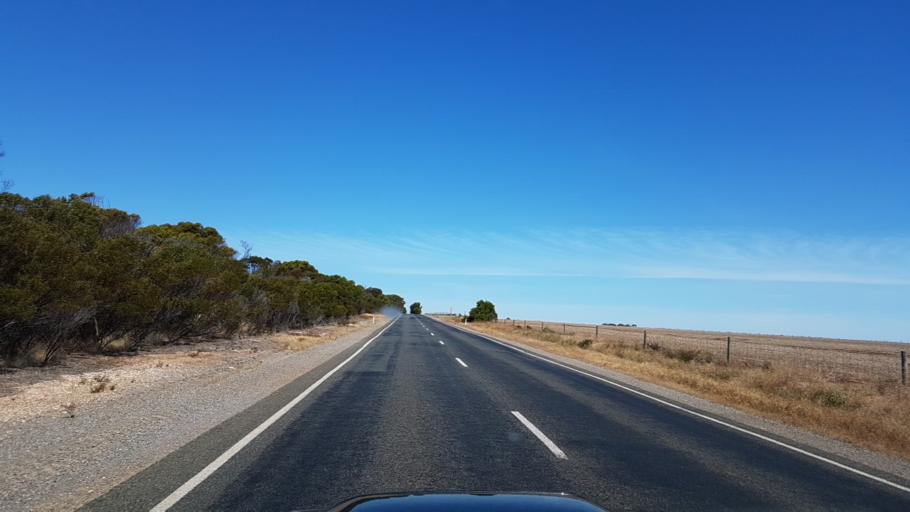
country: AU
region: South Australia
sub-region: Yorke Peninsula
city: Maitland
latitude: -34.3441
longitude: 137.6594
